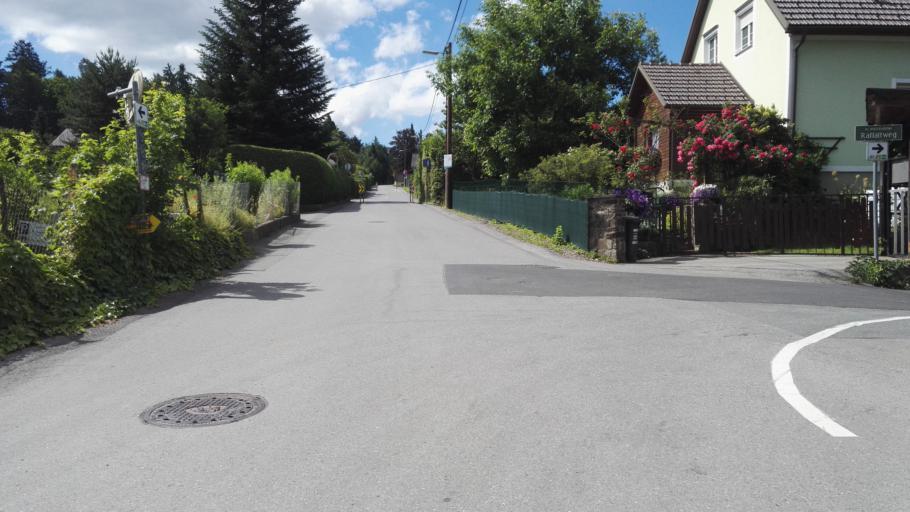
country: AT
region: Styria
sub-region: Graz Stadt
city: Mariatrost
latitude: 47.0766
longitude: 15.4900
